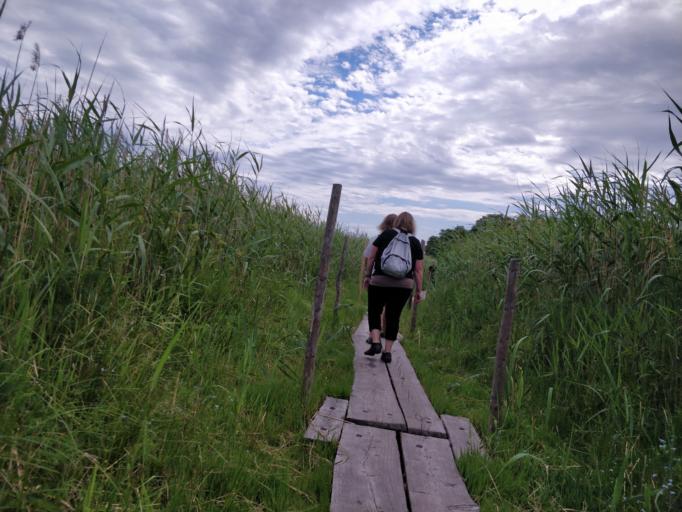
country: FI
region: Uusimaa
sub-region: Helsinki
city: Helsinki
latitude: 60.2064
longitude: 24.9958
